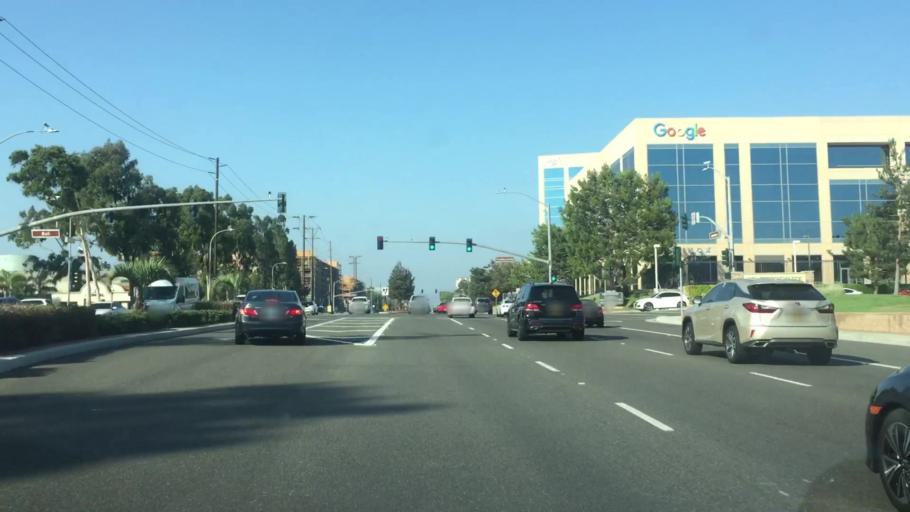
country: US
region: California
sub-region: Orange County
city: Irvine
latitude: 33.6584
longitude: -117.8618
